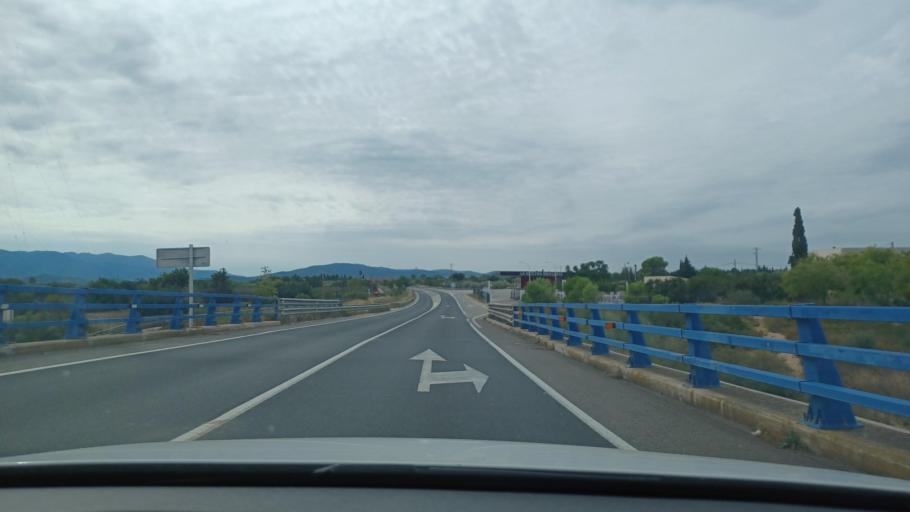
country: ES
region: Catalonia
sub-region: Provincia de Tarragona
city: Santa Barbara
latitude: 40.7392
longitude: 0.5043
